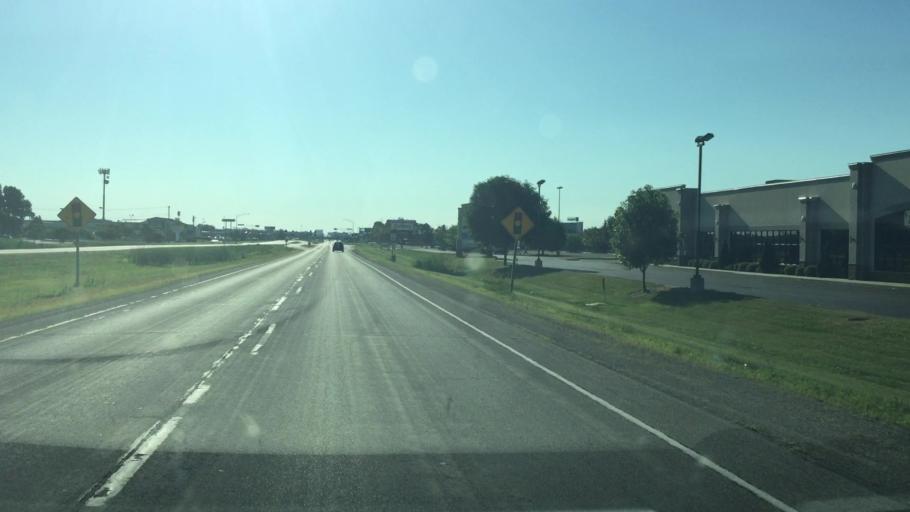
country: US
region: Wisconsin
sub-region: Outagamie County
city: Appleton
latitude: 44.2619
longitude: -88.4803
